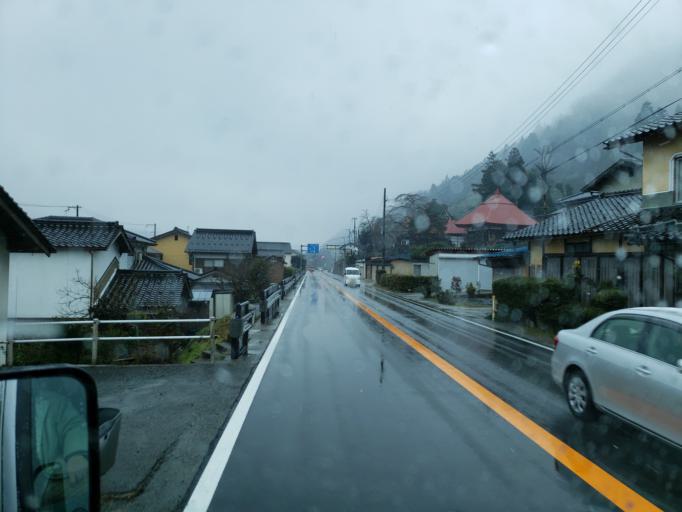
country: JP
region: Hyogo
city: Toyooka
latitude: 35.3848
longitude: 134.7145
